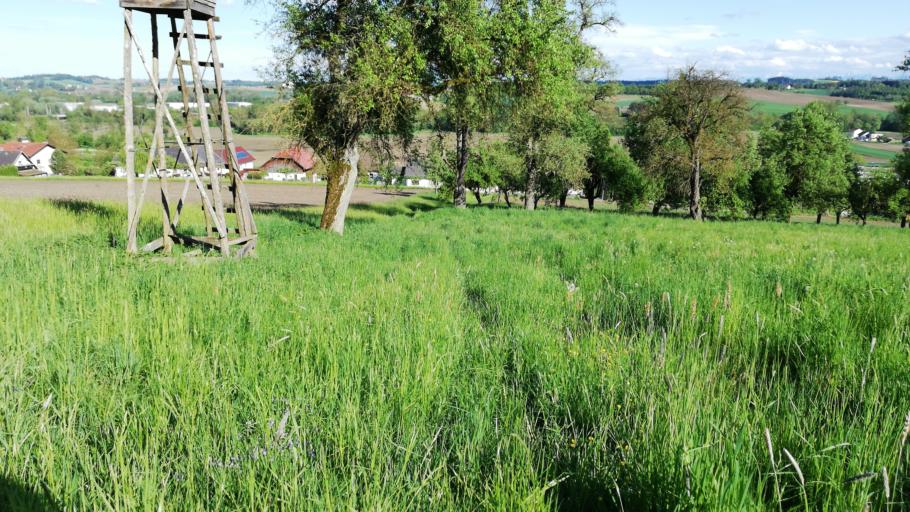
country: AT
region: Upper Austria
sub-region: Politischer Bezirk Grieskirchen
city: Bad Schallerbach
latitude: 48.2208
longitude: 13.9275
